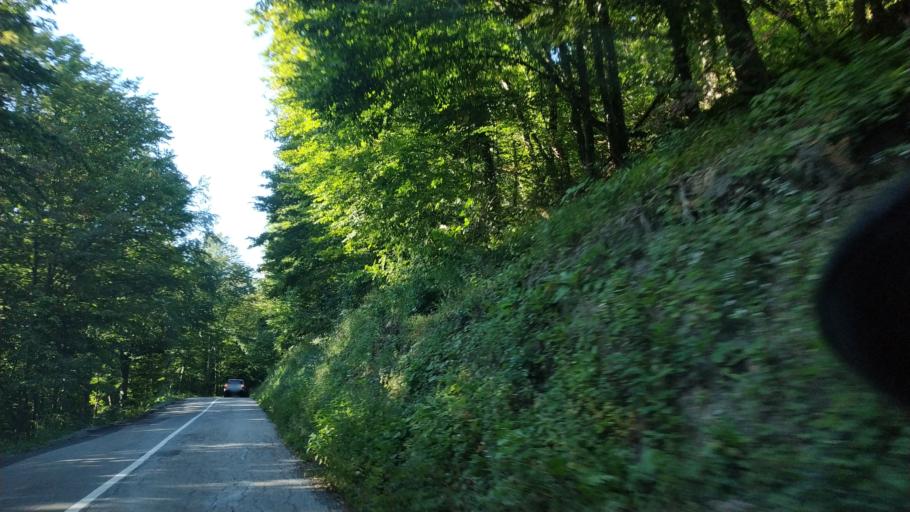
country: RS
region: Central Serbia
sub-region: Rasinski Okrug
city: Krusevac
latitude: 43.4507
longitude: 21.3600
